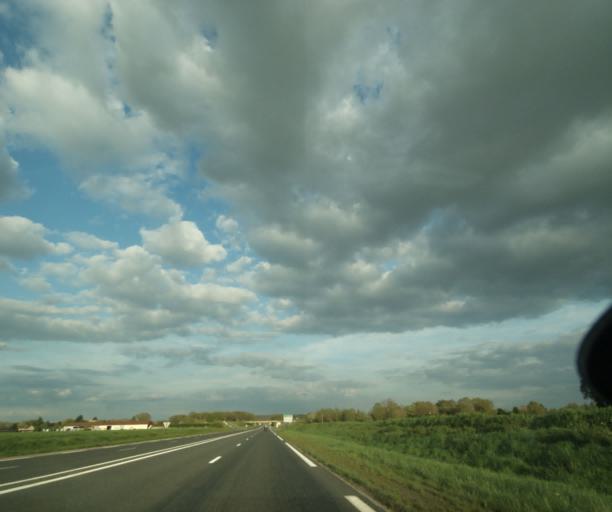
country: FR
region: Ile-de-France
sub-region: Departement de Seine-et-Marne
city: Barbizon
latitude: 48.4563
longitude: 2.5985
